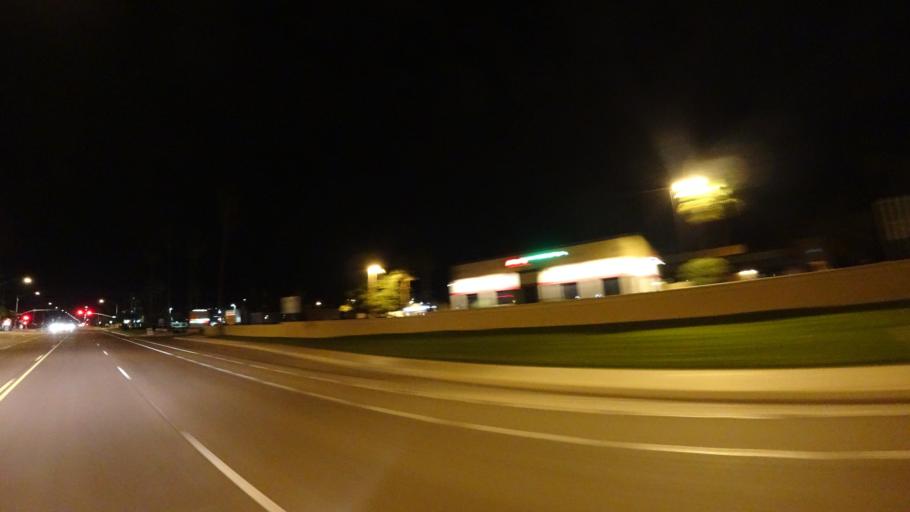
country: US
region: Arizona
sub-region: Maricopa County
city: Mesa
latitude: 33.4356
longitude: -111.7190
